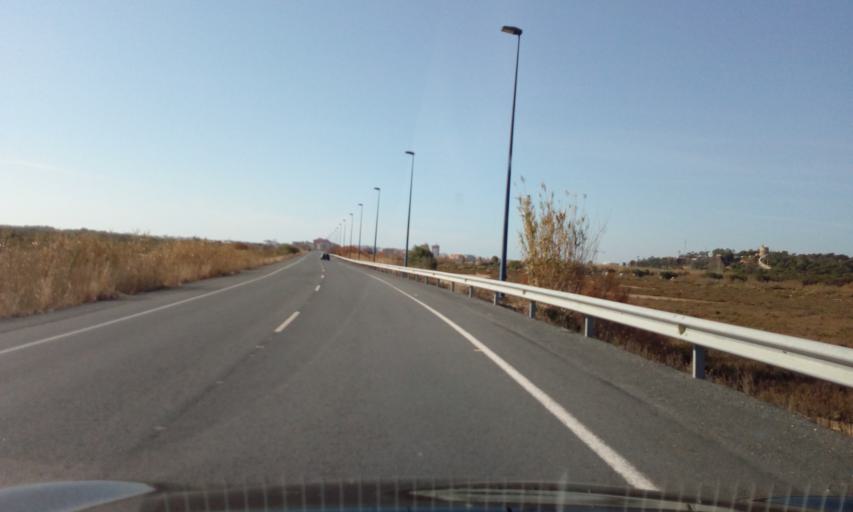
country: ES
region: Andalusia
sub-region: Provincia de Huelva
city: Lepe
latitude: 37.2171
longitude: -7.1882
